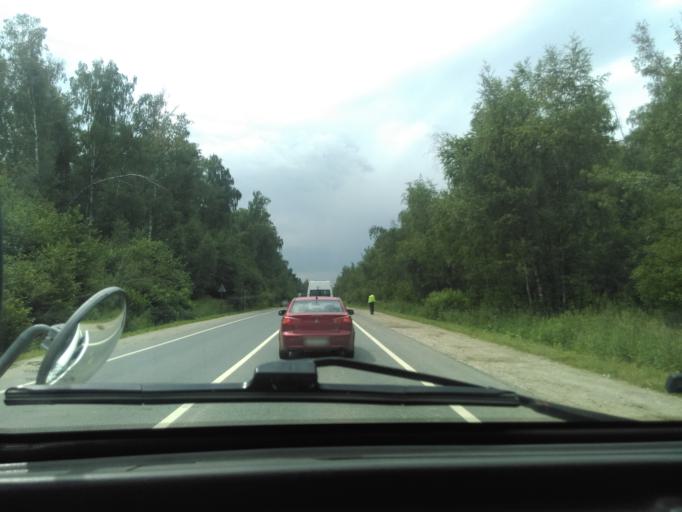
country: RU
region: Moskovskaya
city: Vostryakovo
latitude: 55.4219
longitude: 37.8441
